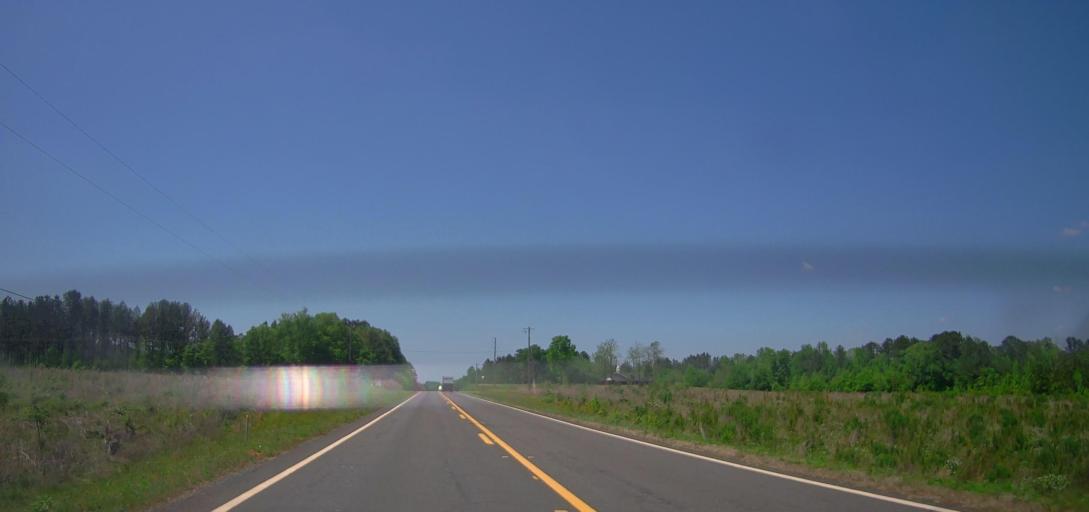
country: US
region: Georgia
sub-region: Jasper County
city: Monticello
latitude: 33.2418
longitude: -83.5538
